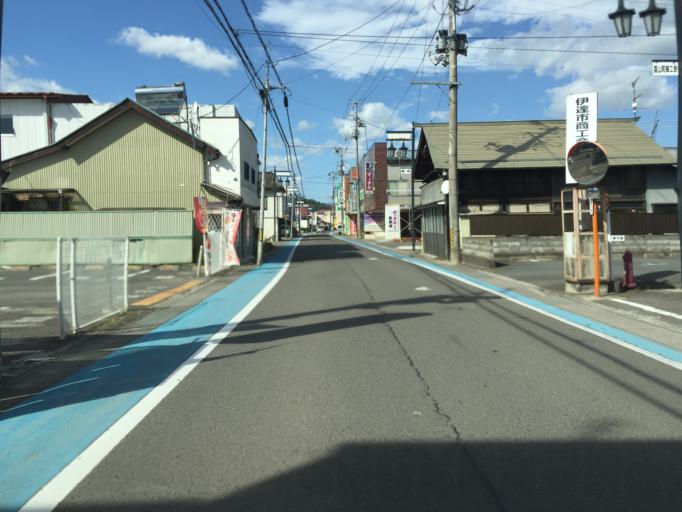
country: JP
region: Fukushima
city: Hobaramachi
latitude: 37.7813
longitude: 140.5949
